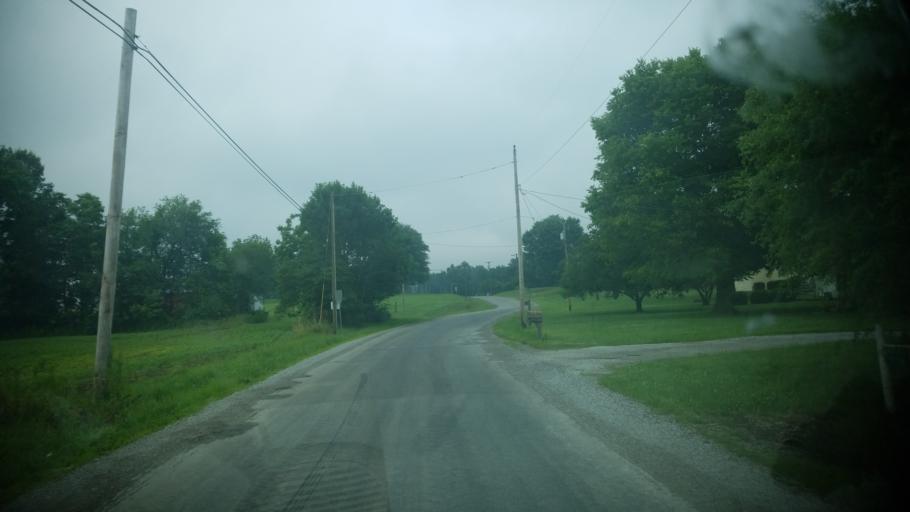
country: US
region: Illinois
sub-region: Clay County
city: Flora
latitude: 38.6765
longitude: -88.3543
